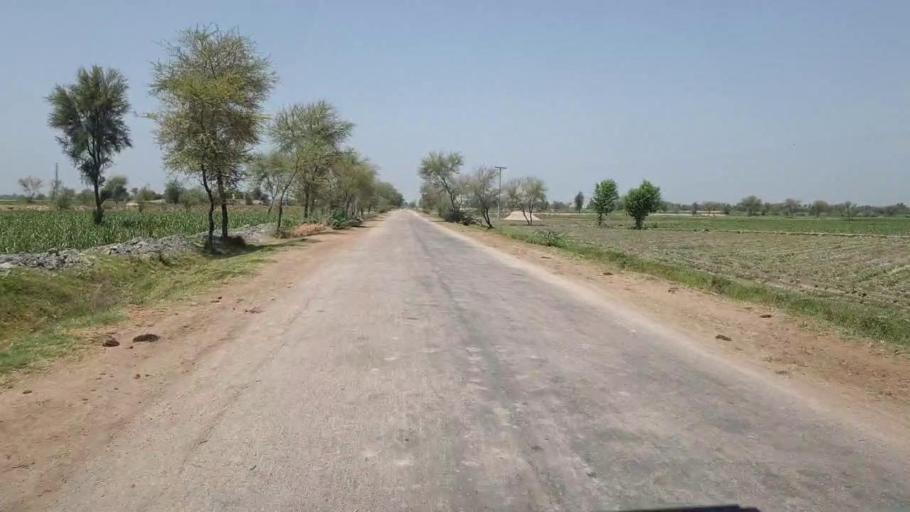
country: PK
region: Sindh
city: Nawabshah
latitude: 26.3484
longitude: 68.3908
